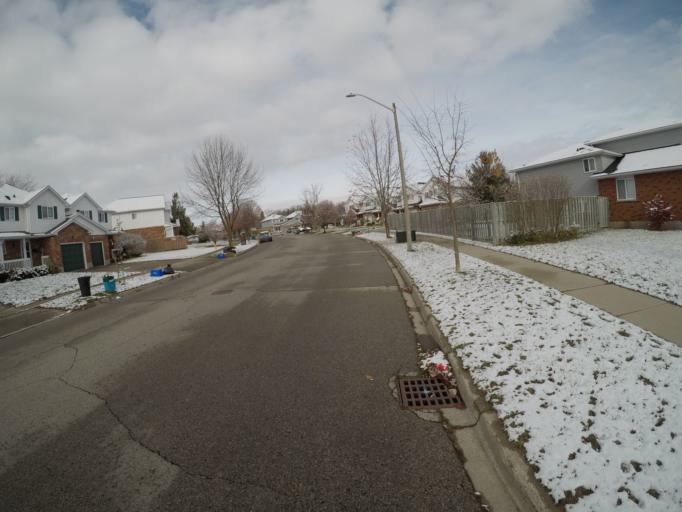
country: CA
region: Ontario
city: Waterloo
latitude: 43.4898
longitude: -80.4908
